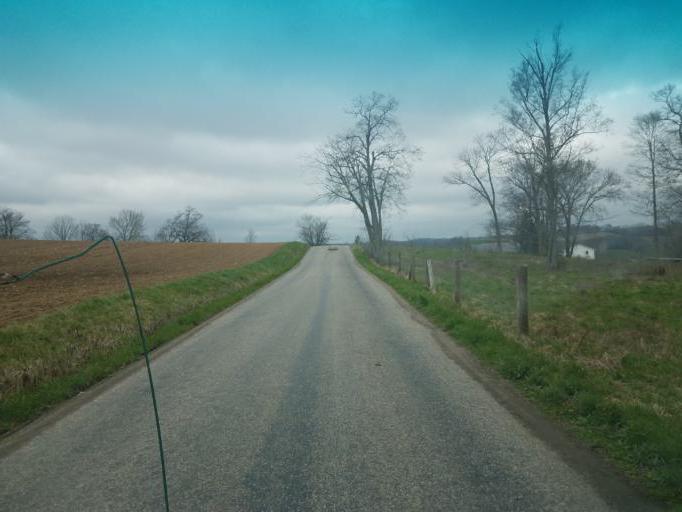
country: US
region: Ohio
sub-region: Stark County
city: Beach City
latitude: 40.6385
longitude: -81.6664
